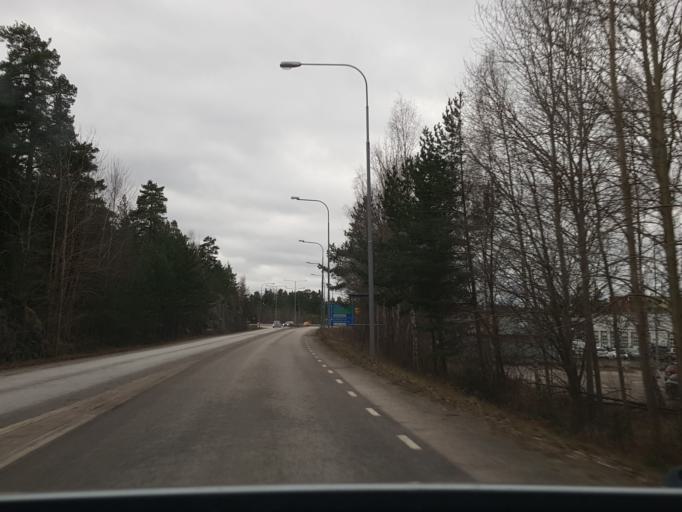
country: SE
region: Stockholm
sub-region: Nacka Kommun
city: Boo
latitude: 59.3256
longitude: 18.2600
